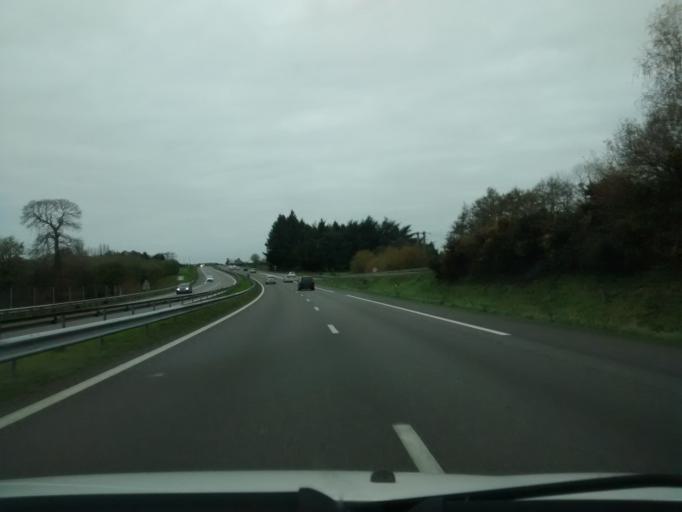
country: FR
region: Brittany
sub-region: Departement d'Ille-et-Vilaine
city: Brece
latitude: 48.1039
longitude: -1.4663
